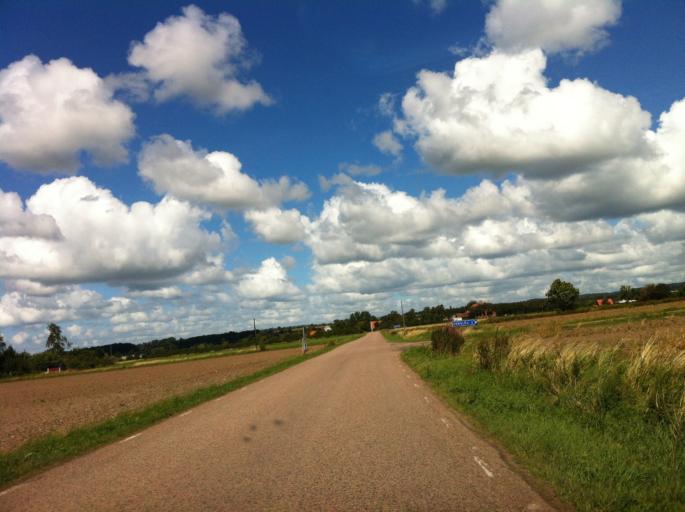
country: SE
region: Skane
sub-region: Angelholms Kommun
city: AEngelholm
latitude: 56.2182
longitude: 12.8577
